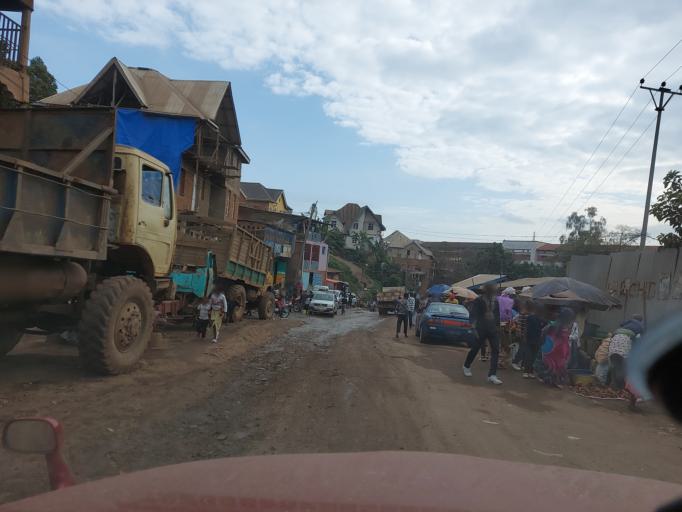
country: CD
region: South Kivu
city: Bukavu
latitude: -2.5085
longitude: 28.8482
